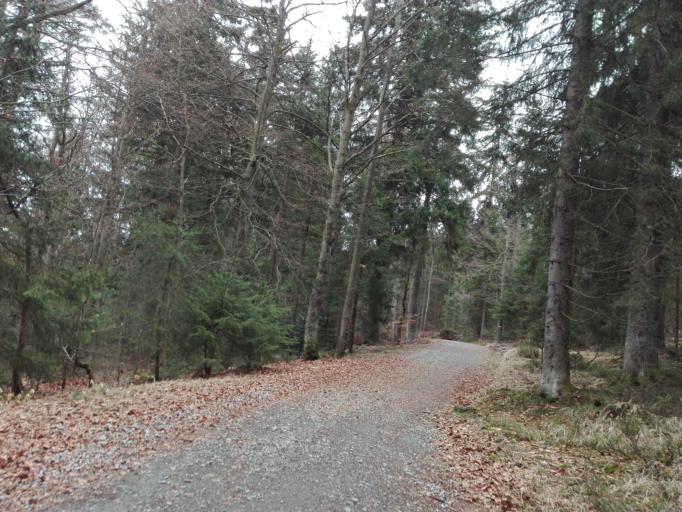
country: AT
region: Upper Austria
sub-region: Politischer Bezirk Rohrbach
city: Aigen im Muehlkreis
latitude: 48.7041
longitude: 13.9650
